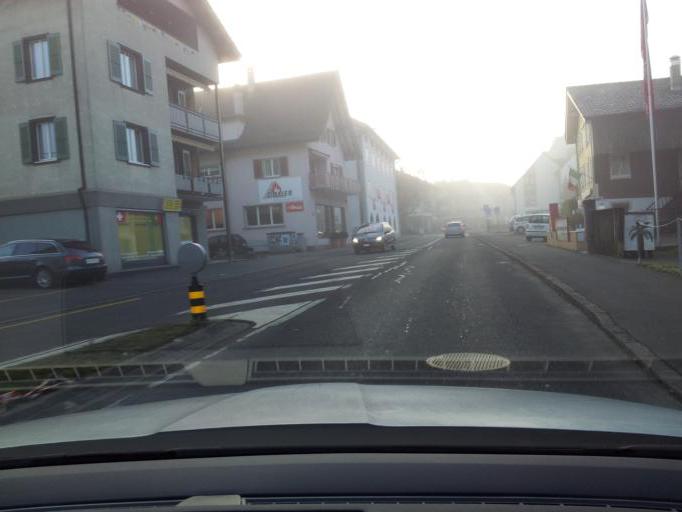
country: CH
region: Obwalden
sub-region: Obwalden
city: Sarnen
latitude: 46.8985
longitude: 8.2462
